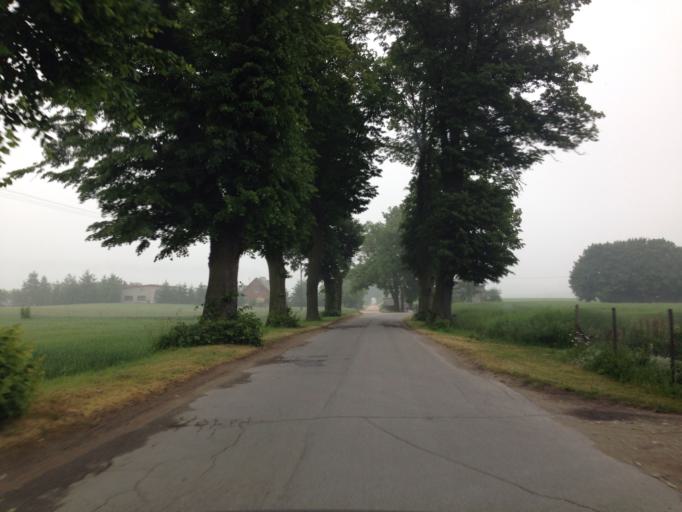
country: PL
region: Kujawsko-Pomorskie
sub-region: Powiat brodnicki
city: Jablonowo Pomorskie
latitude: 53.3863
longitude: 19.2530
